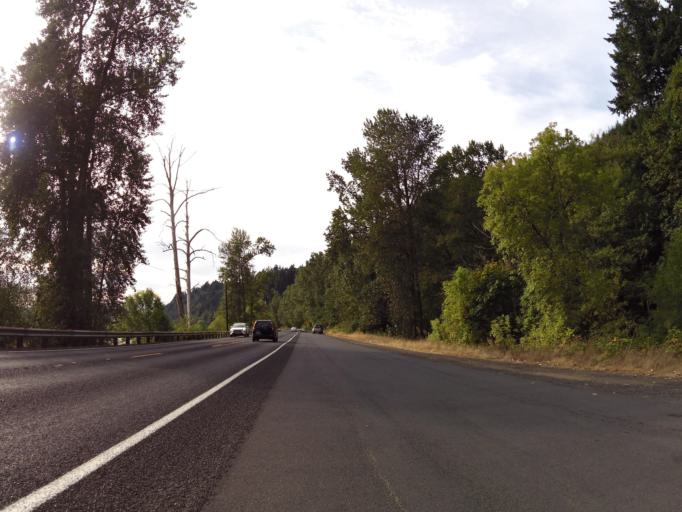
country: US
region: Washington
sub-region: Cowlitz County
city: West Longview
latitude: 46.1862
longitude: -123.0841
